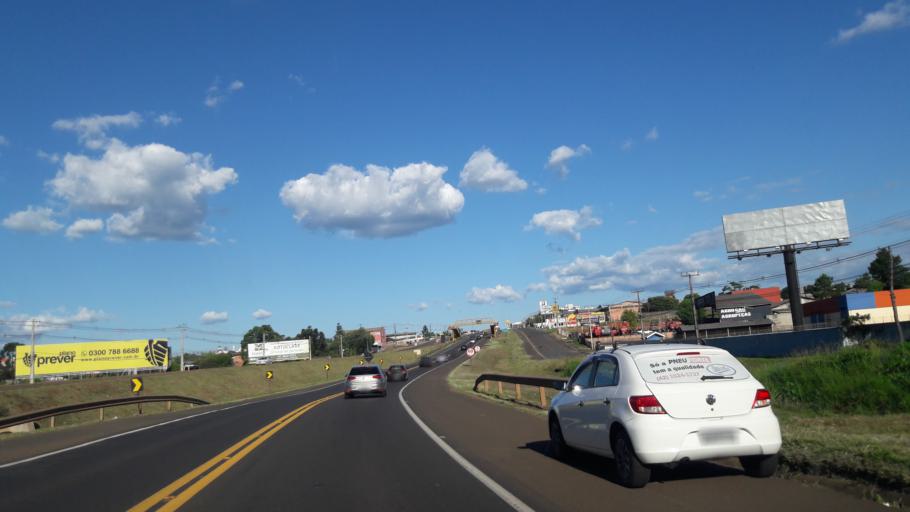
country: BR
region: Parana
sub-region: Guarapuava
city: Guarapuava
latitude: -25.3660
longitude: -51.4911
